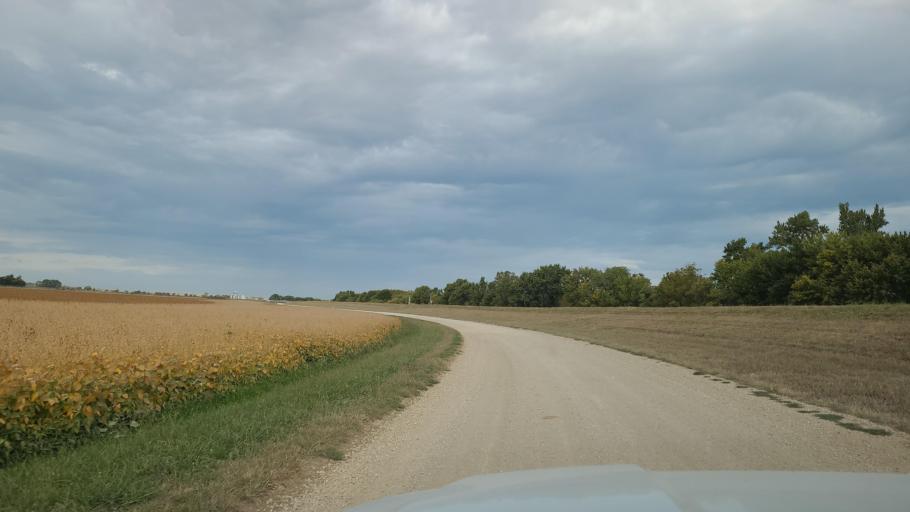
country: US
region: Kansas
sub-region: Douglas County
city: Lawrence
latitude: 39.0177
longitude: -95.2096
